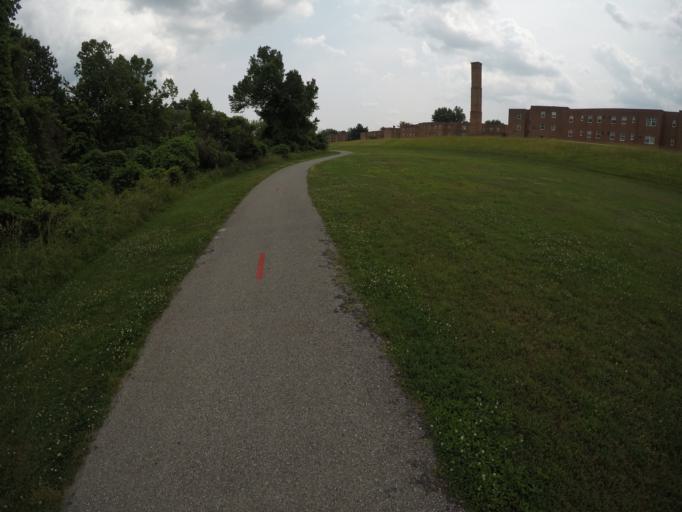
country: US
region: Maryland
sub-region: Prince George's County
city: Brentwood
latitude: 38.9524
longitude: -76.9619
